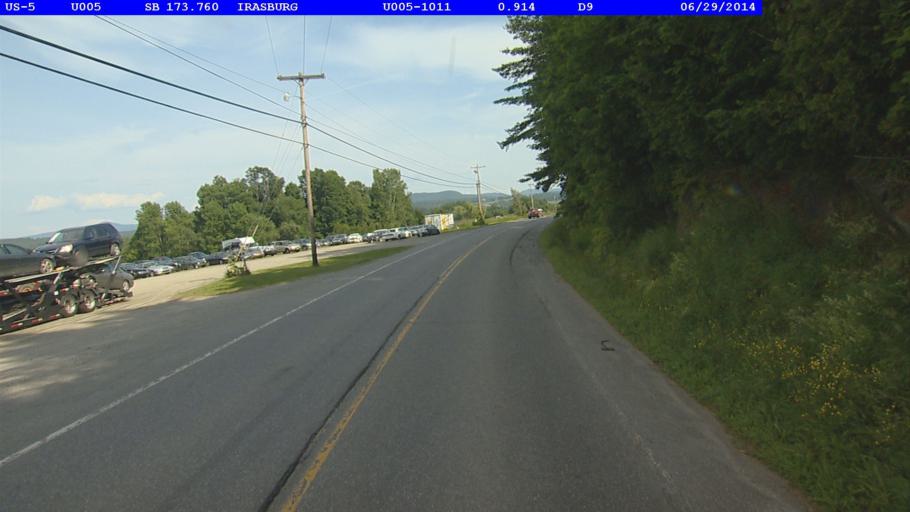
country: US
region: Vermont
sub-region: Orleans County
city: Newport
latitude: 44.8185
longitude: -72.2222
